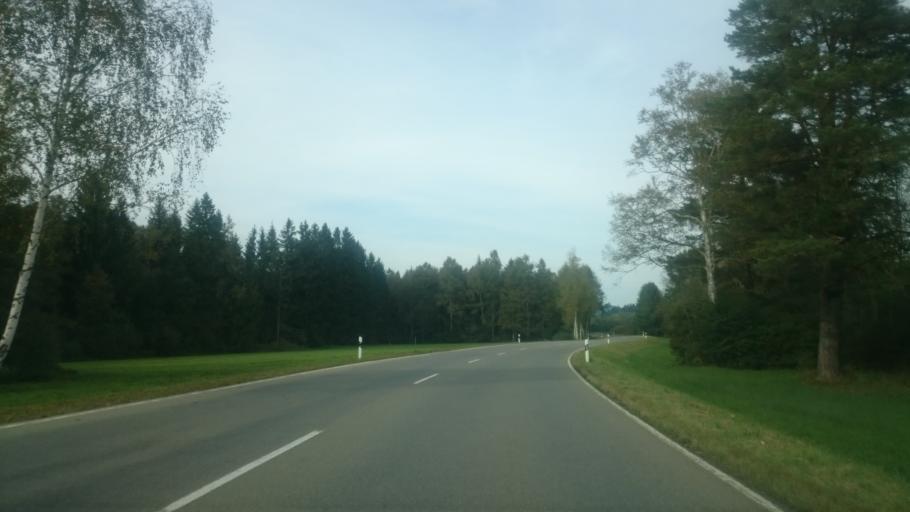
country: AT
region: Tyrol
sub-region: Politischer Bezirk Reutte
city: Vils
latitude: 47.5753
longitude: 10.6533
